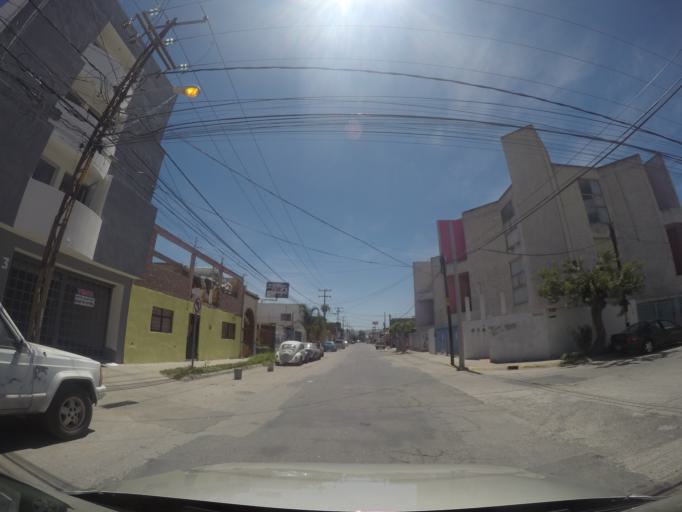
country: MX
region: San Luis Potosi
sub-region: San Luis Potosi
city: San Luis Potosi
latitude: 22.1556
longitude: -100.9967
